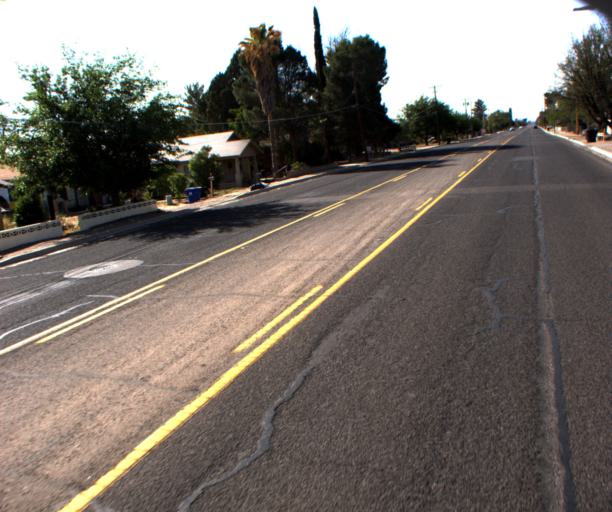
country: US
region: Arizona
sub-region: Graham County
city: Safford
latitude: 32.8291
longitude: -109.7077
